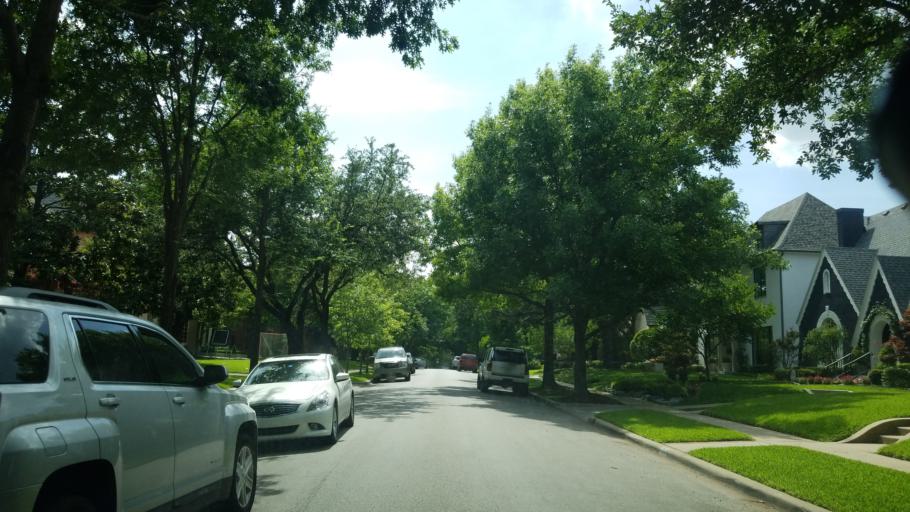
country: US
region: Texas
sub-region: Dallas County
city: University Park
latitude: 32.8530
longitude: -96.8020
